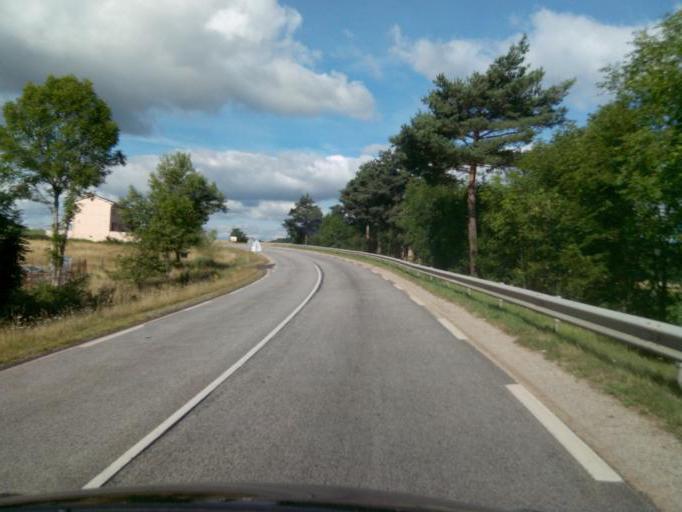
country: FR
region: Auvergne
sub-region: Departement de la Haute-Loire
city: Retournac
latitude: 45.2262
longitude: 4.0346
